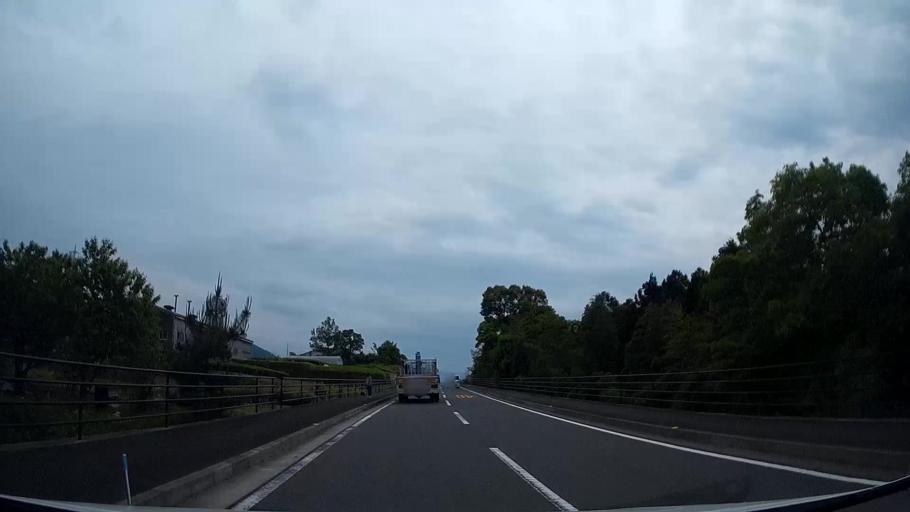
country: JP
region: Shizuoka
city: Ito
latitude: 34.9662
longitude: 138.9469
